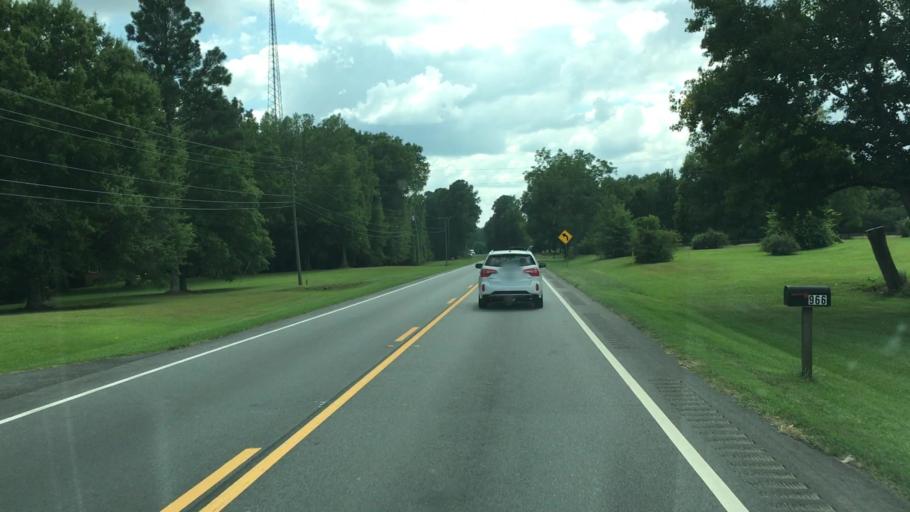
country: US
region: Georgia
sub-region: Putnam County
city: Eatonton
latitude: 33.3836
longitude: -83.3773
